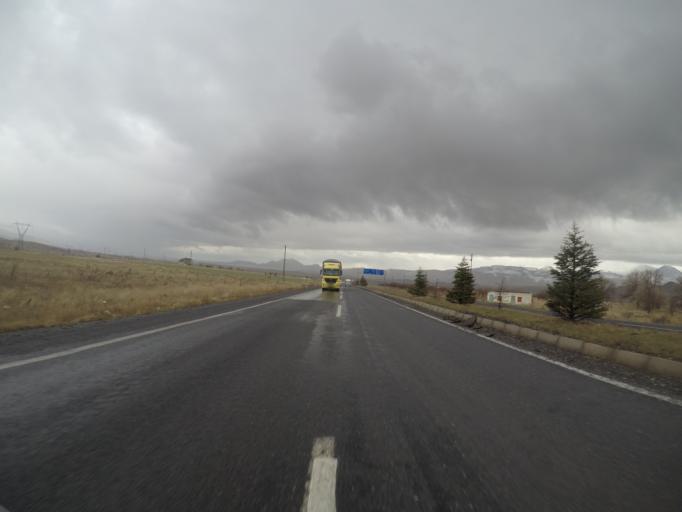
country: TR
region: Kayseri
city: Incesu
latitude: 38.6810
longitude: 35.2270
